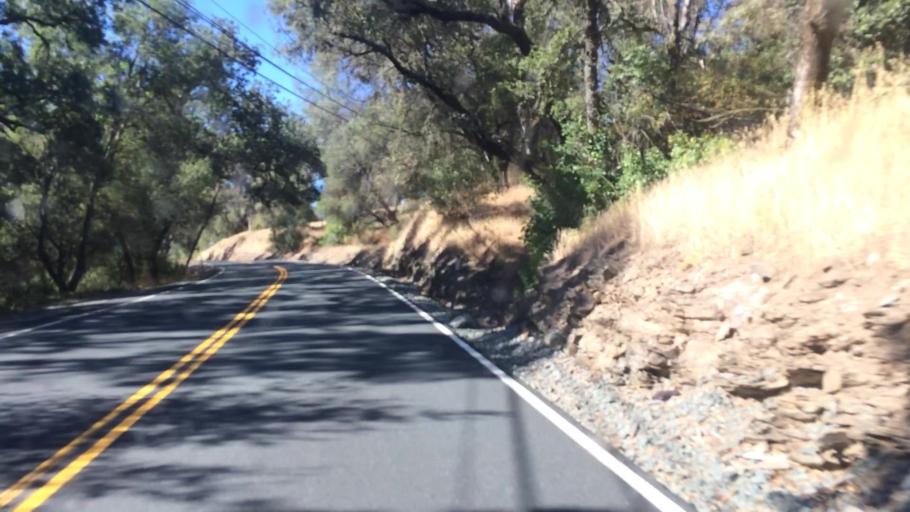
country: US
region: California
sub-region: Amador County
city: Plymouth
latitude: 38.5674
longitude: -120.8462
